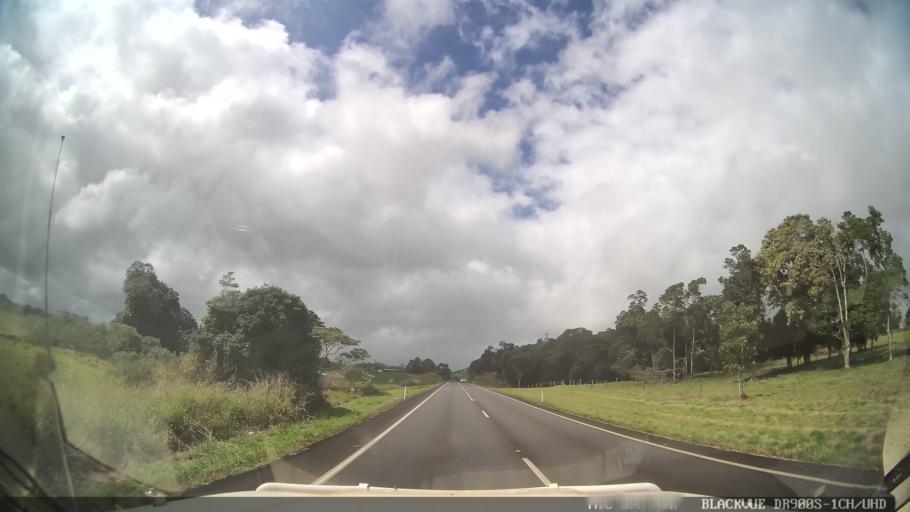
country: AU
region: Queensland
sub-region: Tablelands
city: Atherton
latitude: -17.3037
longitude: 145.6233
